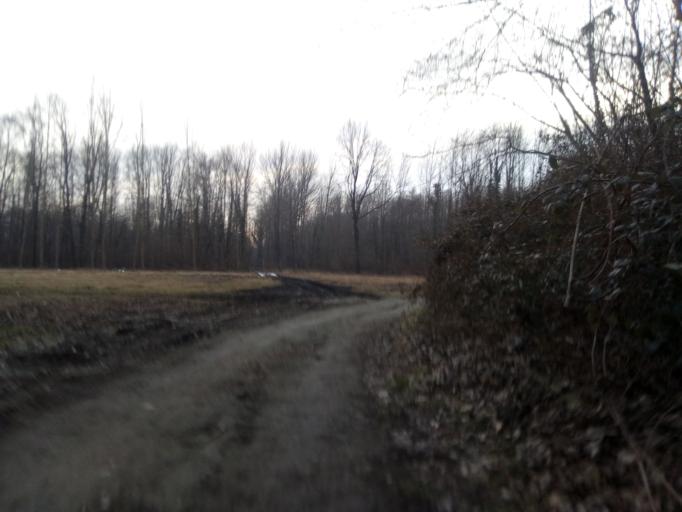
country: IT
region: Piedmont
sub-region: Provincia di Torino
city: Cascinette d'Ivrea
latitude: 45.4901
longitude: 7.9149
